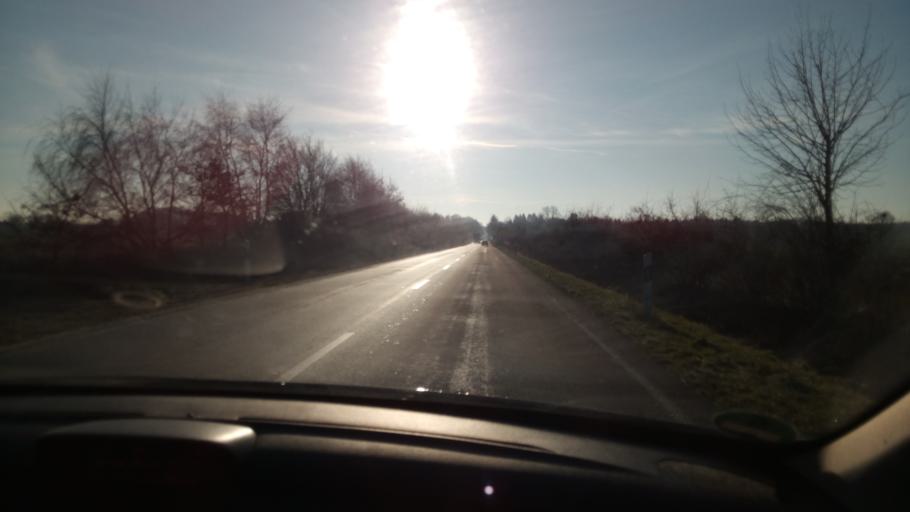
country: DE
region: Schleswig-Holstein
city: Dalldorf
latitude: 53.4437
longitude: 10.6085
